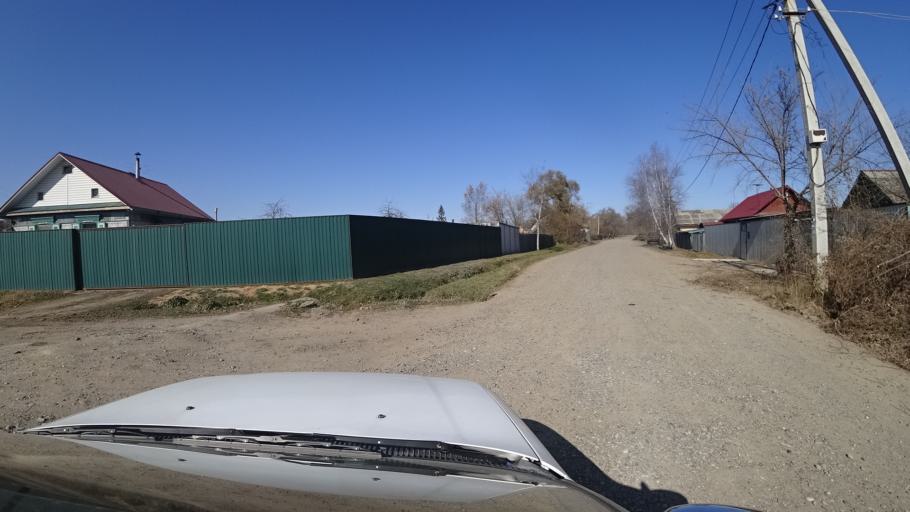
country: RU
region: Primorskiy
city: Dal'nerechensk
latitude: 45.9306
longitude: 133.7539
